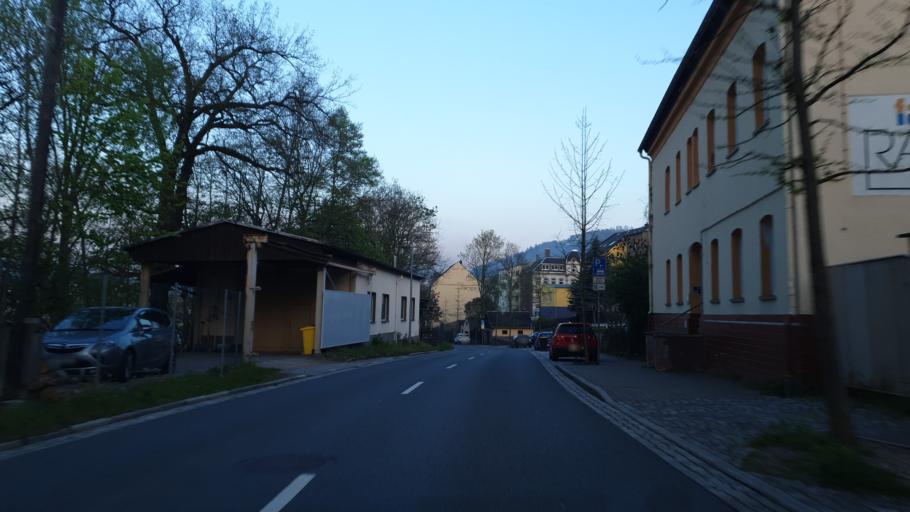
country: DE
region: Saxony
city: Aue
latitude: 50.5909
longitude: 12.6949
